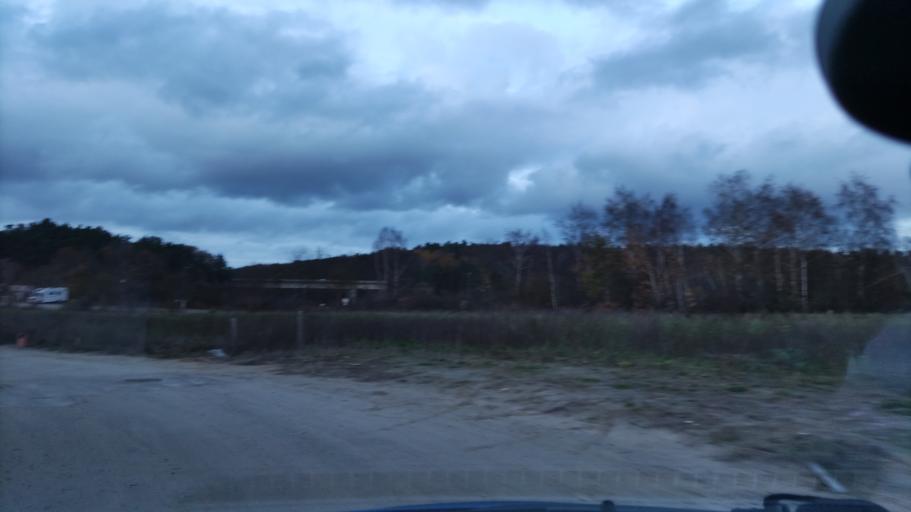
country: DE
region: Lower Saxony
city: Bad Bevensen
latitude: 53.0726
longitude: 10.6018
